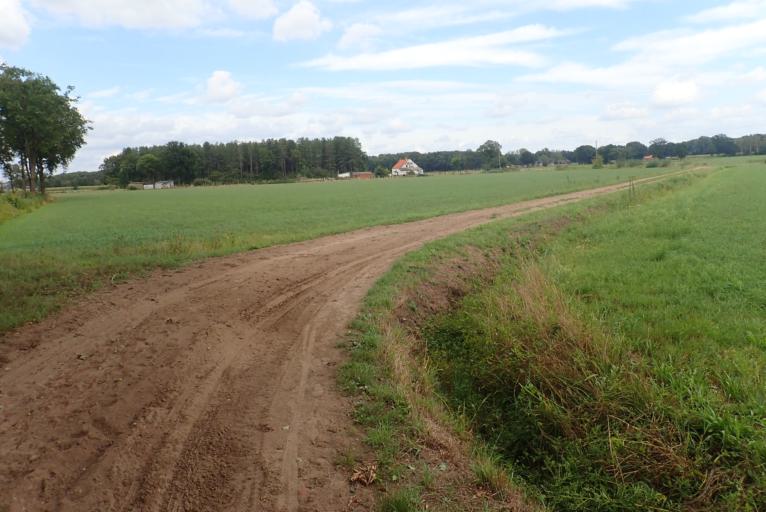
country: BE
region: Flanders
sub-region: Provincie Antwerpen
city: Lille
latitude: 51.2308
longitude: 4.7968
